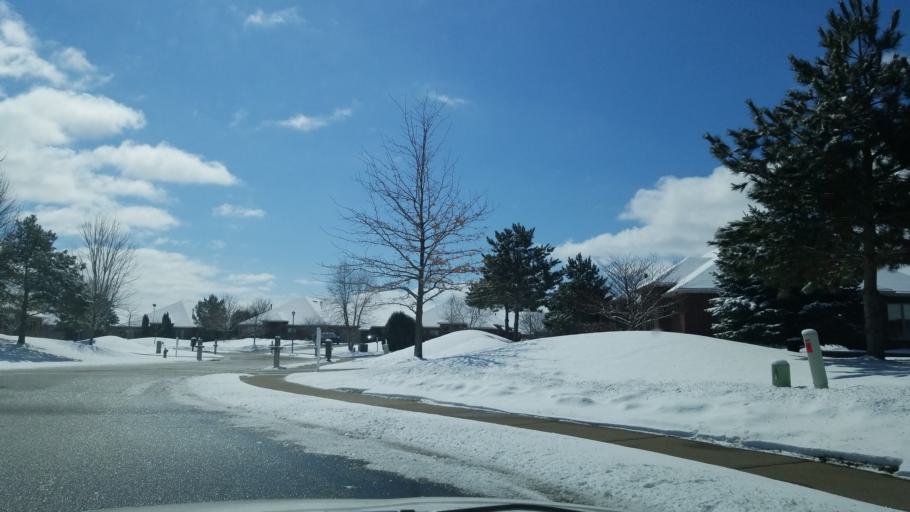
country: US
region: Wisconsin
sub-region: Saint Croix County
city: Hudson
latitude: 44.9591
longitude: -92.7090
